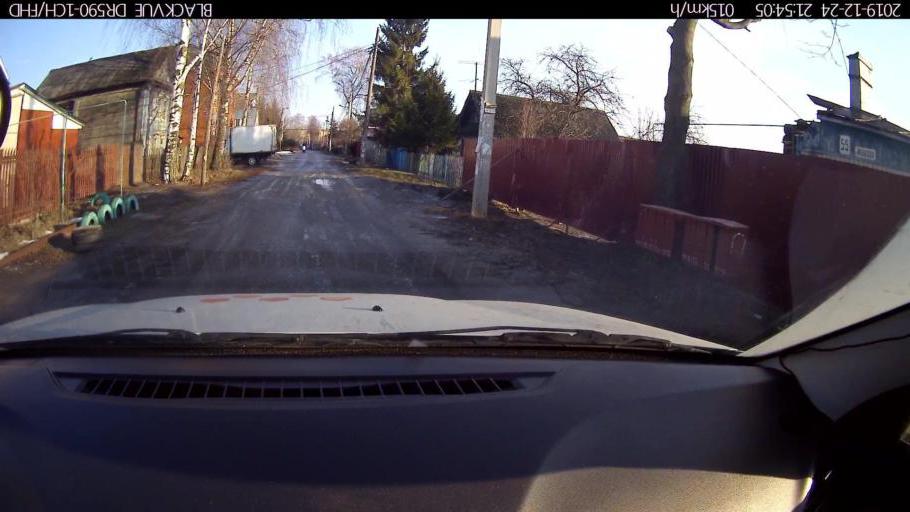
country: RU
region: Nizjnij Novgorod
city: Burevestnik
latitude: 56.2169
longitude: 43.8442
